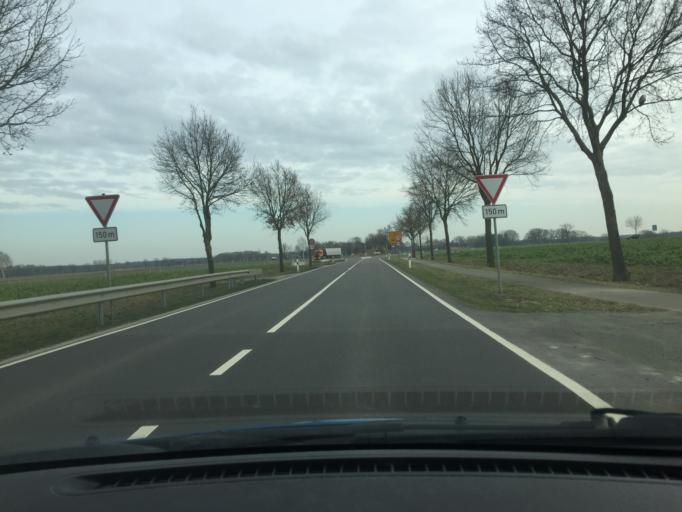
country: DE
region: Lower Saxony
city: Waddeweitz
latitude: 52.9889
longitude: 10.9778
